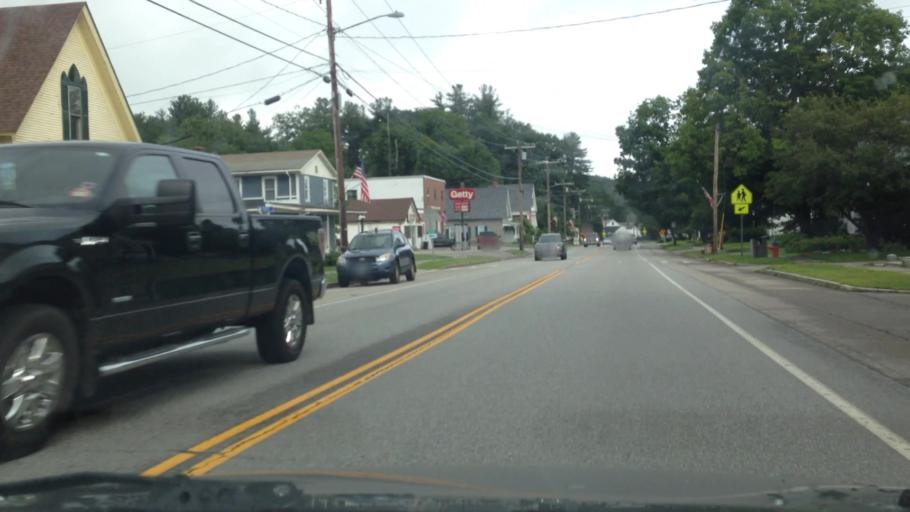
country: US
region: New Hampshire
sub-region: Cheshire County
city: Marlborough
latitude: 42.9046
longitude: -72.2091
